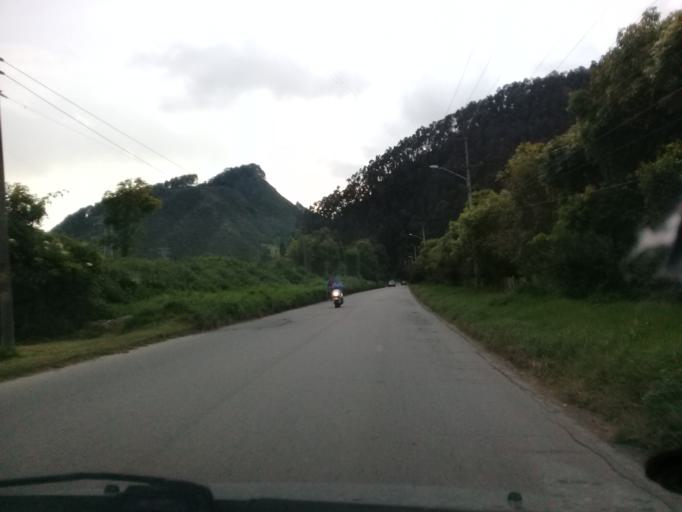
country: CO
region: Cundinamarca
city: Cajica
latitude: 4.9267
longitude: -74.0602
